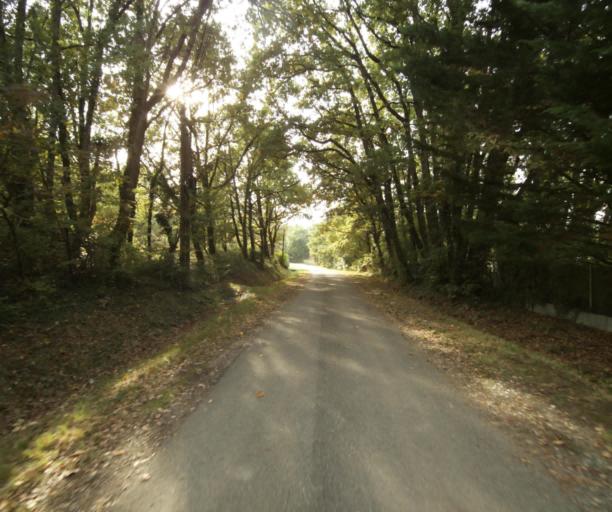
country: FR
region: Midi-Pyrenees
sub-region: Departement du Tarn-et-Garonne
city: Campsas
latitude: 43.8931
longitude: 1.3209
